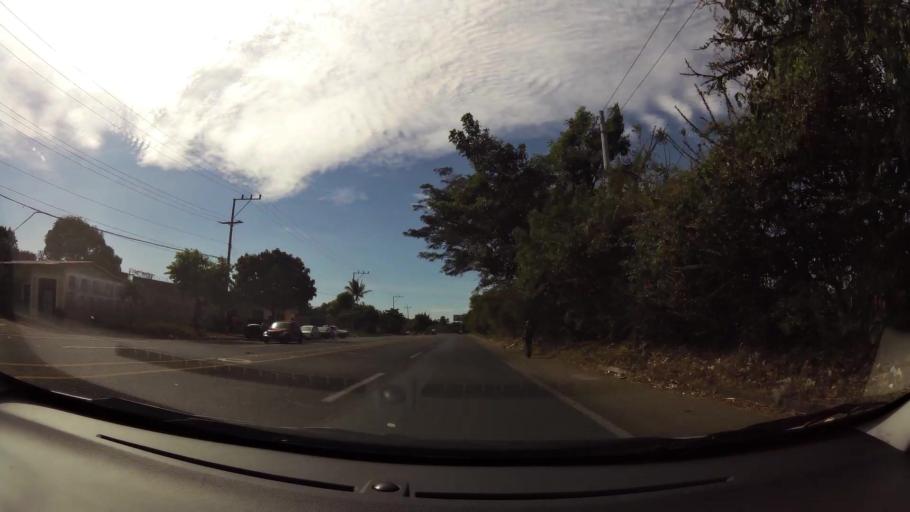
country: SV
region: Santa Ana
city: Chalchuapa
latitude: 13.9881
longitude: -89.6867
